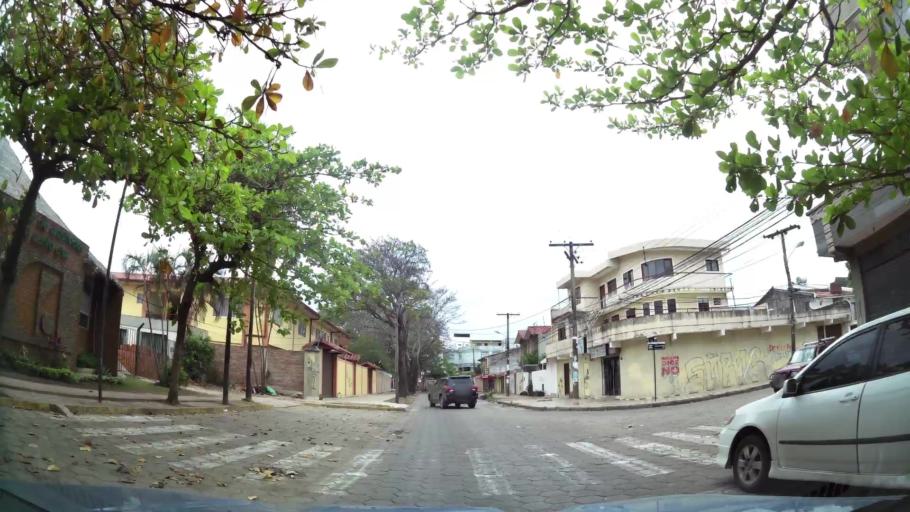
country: BO
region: Santa Cruz
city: Santa Cruz de la Sierra
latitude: -17.7743
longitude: -63.1707
